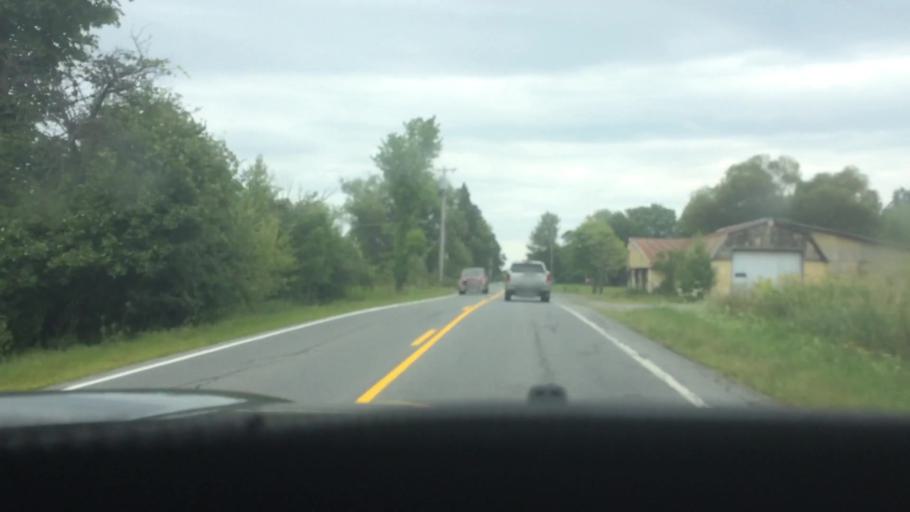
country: US
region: New York
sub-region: St. Lawrence County
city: Canton
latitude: 44.5374
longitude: -75.1681
